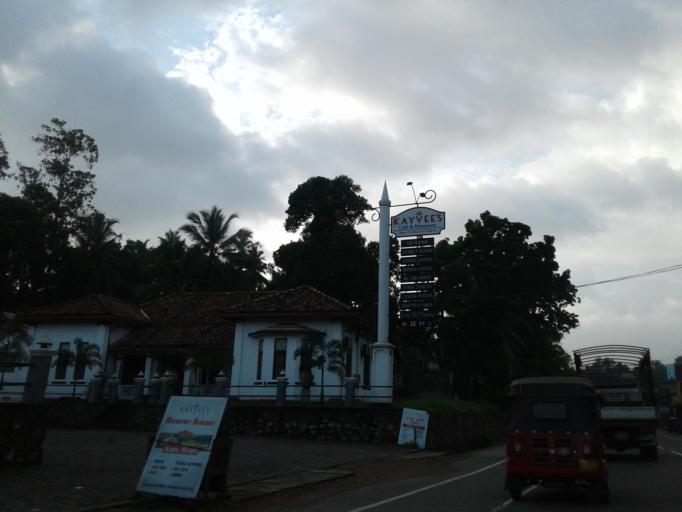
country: LK
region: Western
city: Mulleriyawa
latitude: 6.9309
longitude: 79.9824
